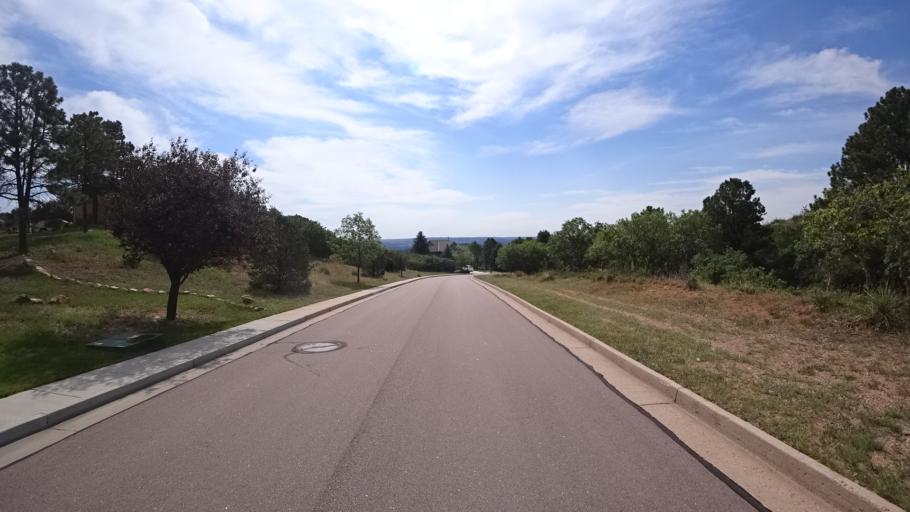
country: US
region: Colorado
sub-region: El Paso County
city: Air Force Academy
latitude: 38.9534
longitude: -104.8679
